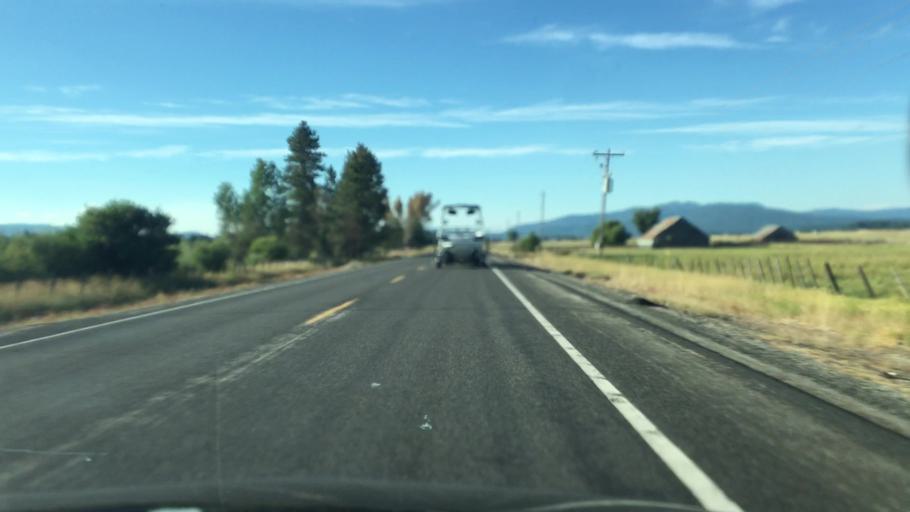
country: US
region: Idaho
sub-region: Valley County
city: Cascade
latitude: 44.4295
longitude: -115.9995
